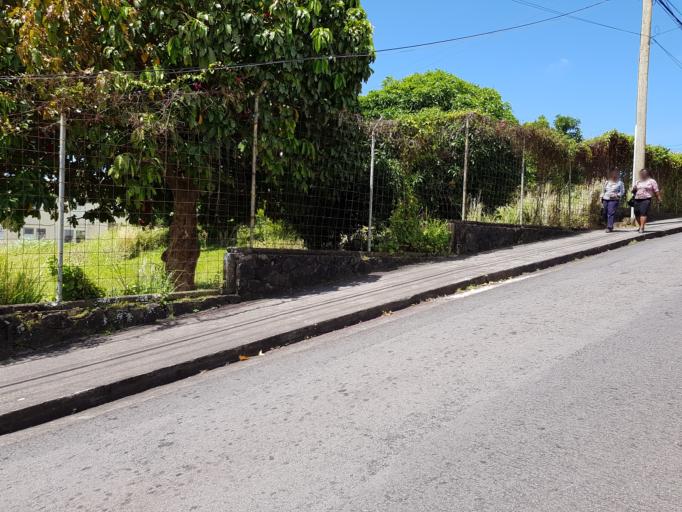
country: VC
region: Saint George
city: Kingstown
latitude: 13.1579
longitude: -61.2264
